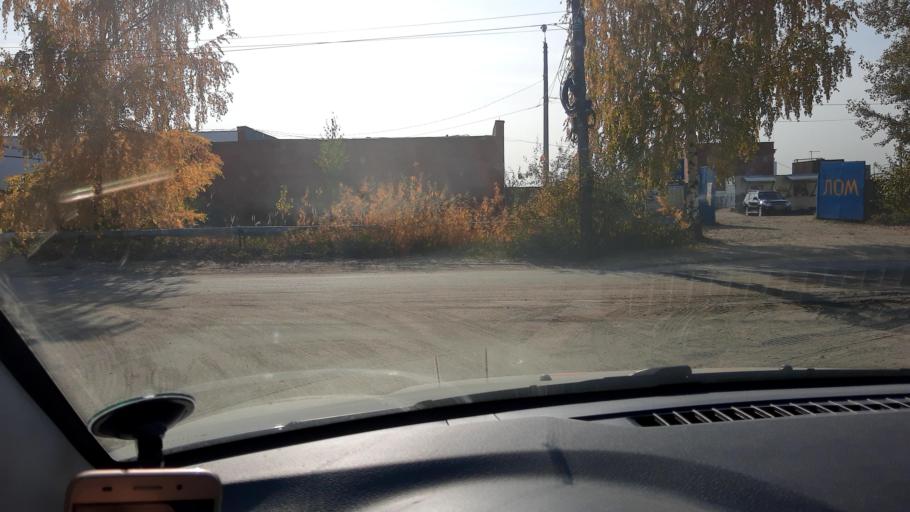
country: RU
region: Nizjnij Novgorod
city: Gorbatovka
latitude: 56.3559
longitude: 43.8015
